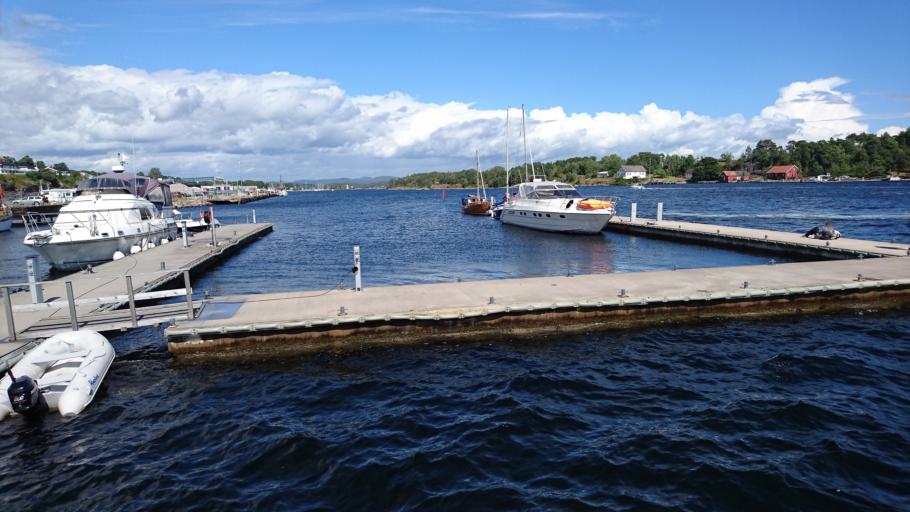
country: NO
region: Telemark
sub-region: Bamble
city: Langesund
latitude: 59.0011
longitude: 9.7506
